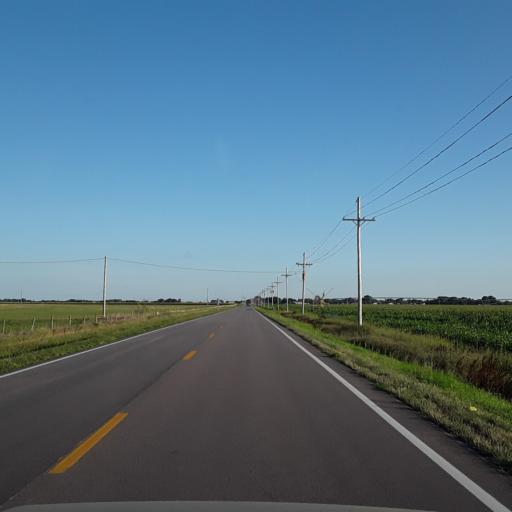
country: US
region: Nebraska
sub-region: Hall County
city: Grand Island
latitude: 40.9586
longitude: -98.3207
